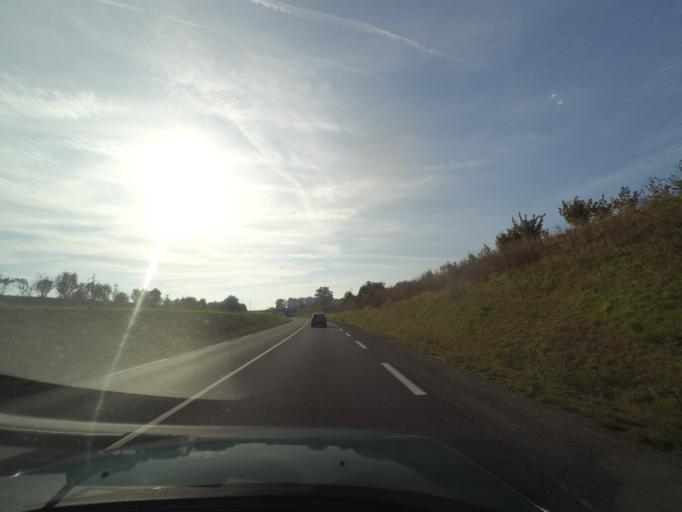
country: FR
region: Pays de la Loire
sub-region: Departement de la Vendee
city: Bouffere
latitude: 46.9657
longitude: -1.3278
